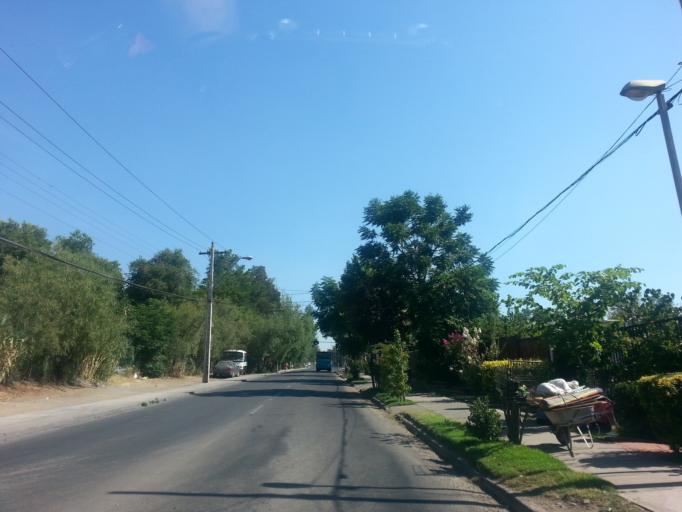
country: CL
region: Santiago Metropolitan
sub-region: Provincia de Santiago
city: Villa Presidente Frei, Nunoa, Santiago, Chile
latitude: -33.4208
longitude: -70.5297
